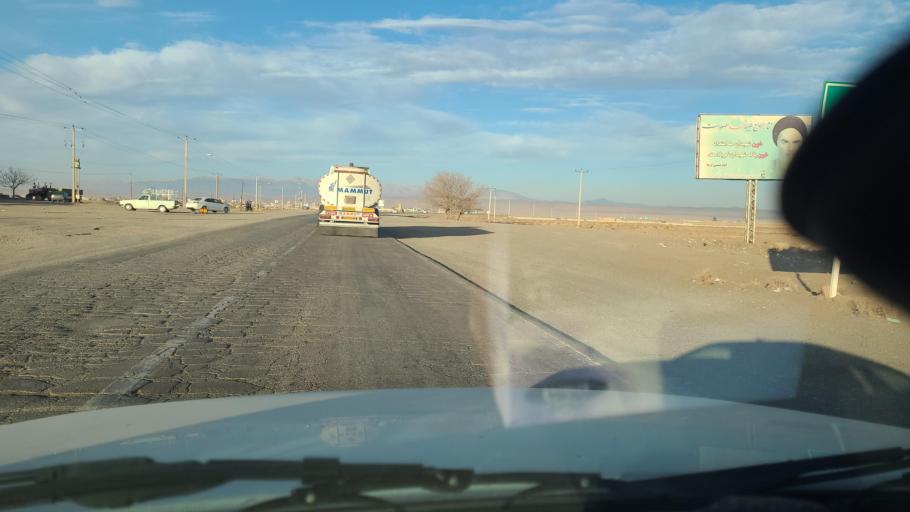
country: IR
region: Razavi Khorasan
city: Neqab
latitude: 36.6098
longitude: 57.5936
